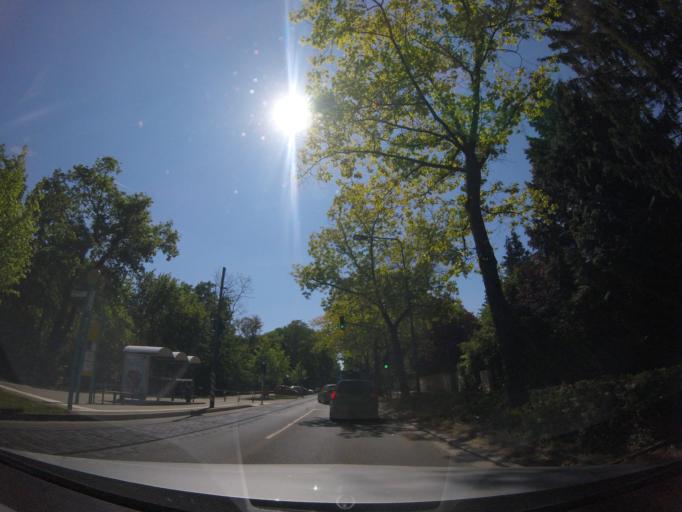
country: DE
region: Hesse
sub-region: Regierungsbezirk Darmstadt
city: Frankfurt am Main
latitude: 50.0876
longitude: 8.6672
